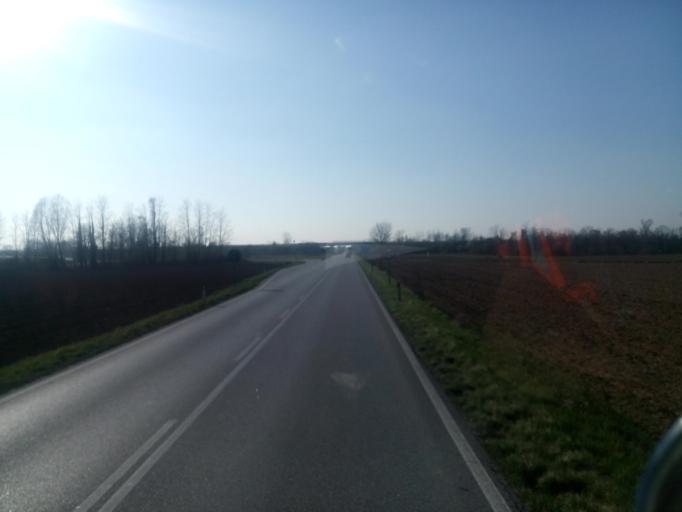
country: IT
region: Friuli Venezia Giulia
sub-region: Provincia di Udine
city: Bertiolo
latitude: 45.9440
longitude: 13.0898
